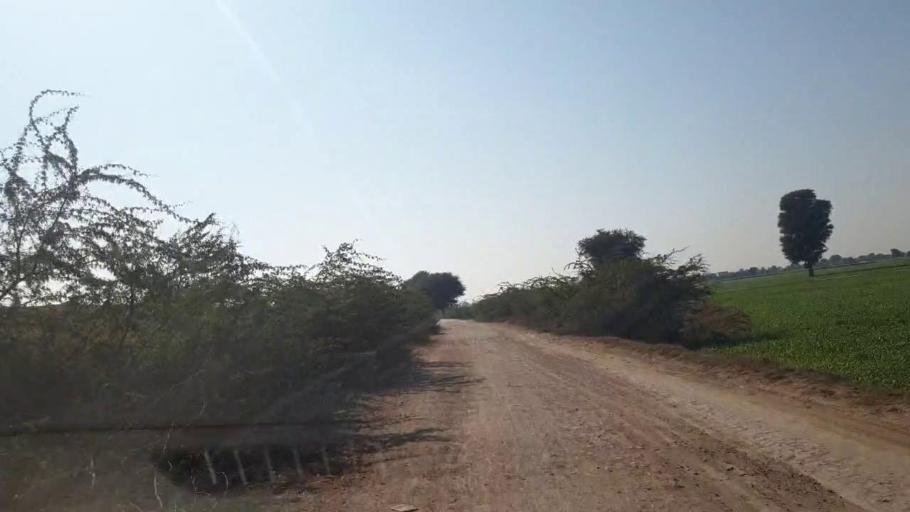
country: PK
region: Sindh
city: Shahpur Chakar
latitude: 26.0848
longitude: 68.6472
